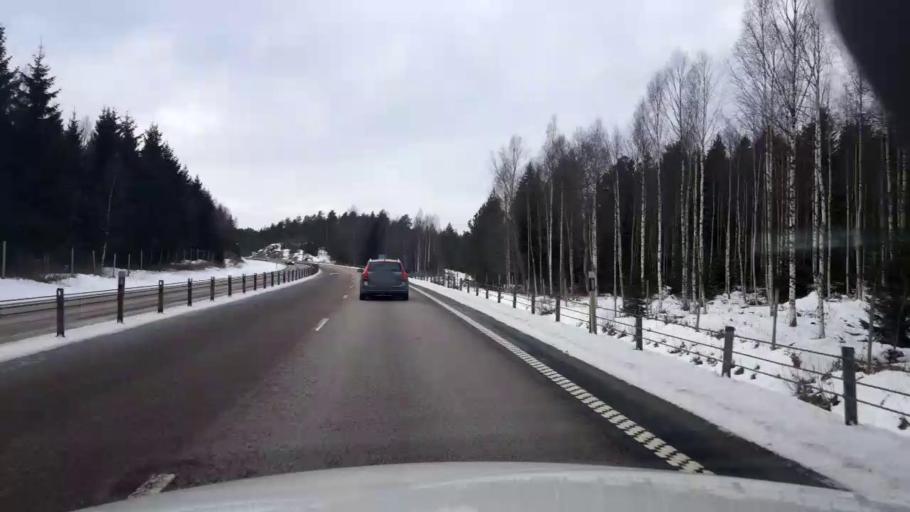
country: SE
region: Gaevleborg
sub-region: Hudiksvalls Kommun
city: Hudiksvall
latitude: 61.7894
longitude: 17.1431
